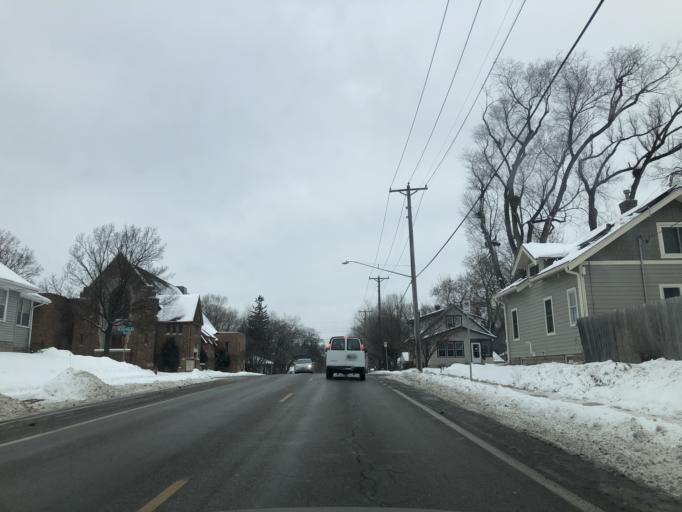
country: US
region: Minnesota
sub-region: Hennepin County
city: Robbinsdale
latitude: 45.0241
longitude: -93.3116
